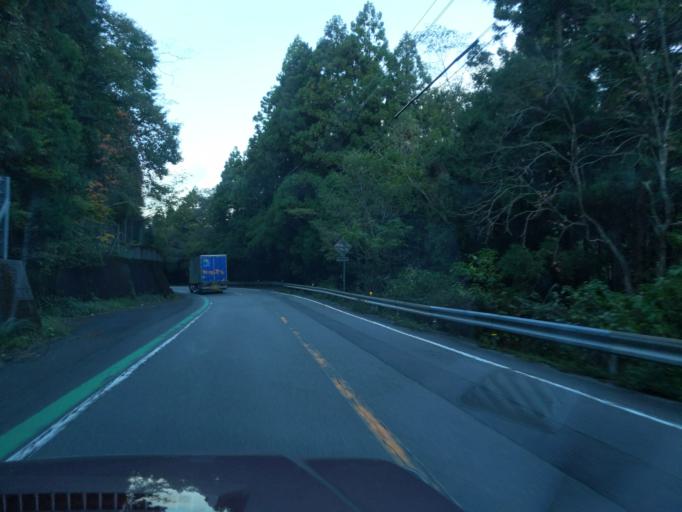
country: JP
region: Tokushima
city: Anan
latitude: 33.7067
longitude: 134.4544
